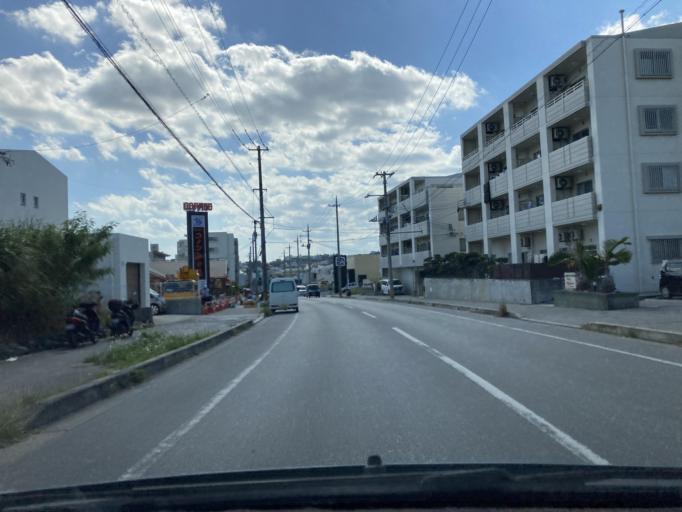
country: JP
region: Okinawa
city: Tomigusuku
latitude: 26.1901
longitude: 127.7113
